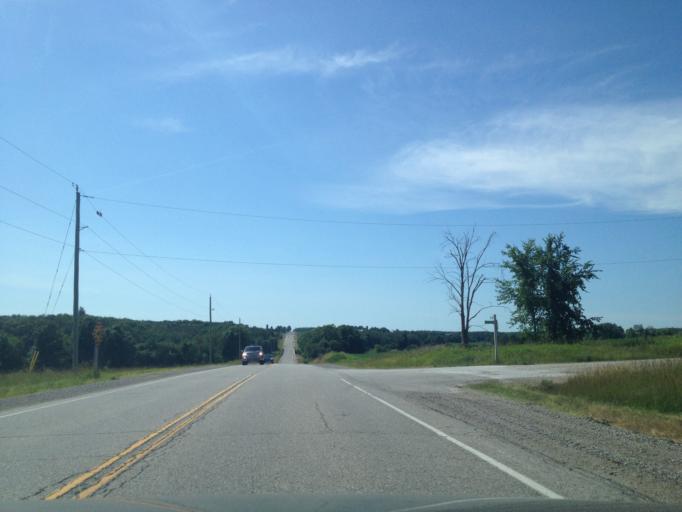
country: CA
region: Ontario
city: Stratford
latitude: 43.4815
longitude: -80.8286
